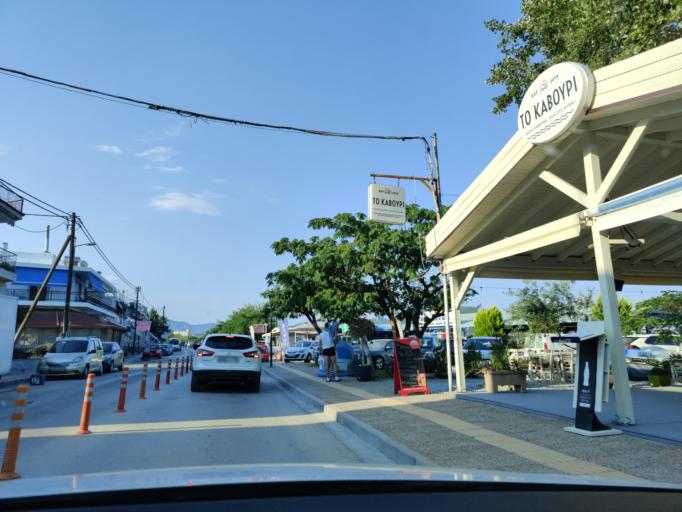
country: GR
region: East Macedonia and Thrace
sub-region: Nomos Kavalas
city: Nea Peramos
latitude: 40.8340
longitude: 24.3048
